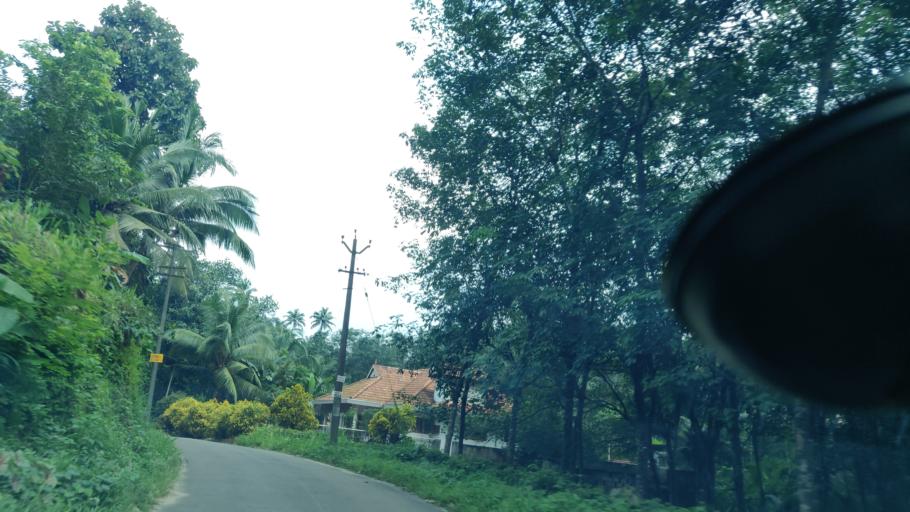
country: IN
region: Kerala
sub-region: Kottayam
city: Lalam
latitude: 9.8418
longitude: 76.7077
